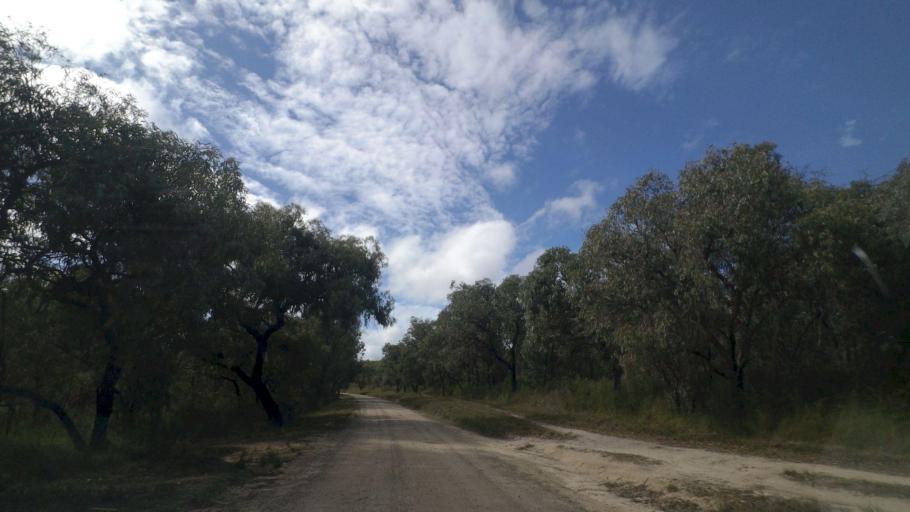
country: AU
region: Victoria
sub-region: Cardinia
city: Gembrook
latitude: -37.9964
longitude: 145.6180
